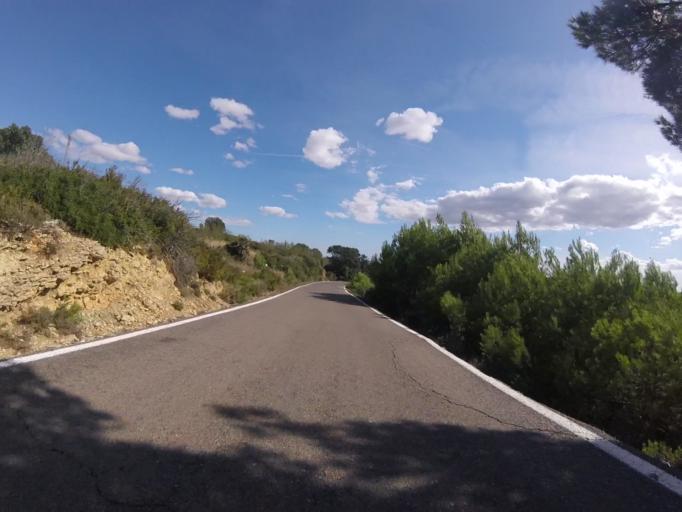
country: ES
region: Valencia
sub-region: Provincia de Castello
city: Albocasser
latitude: 40.3964
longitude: 0.0899
